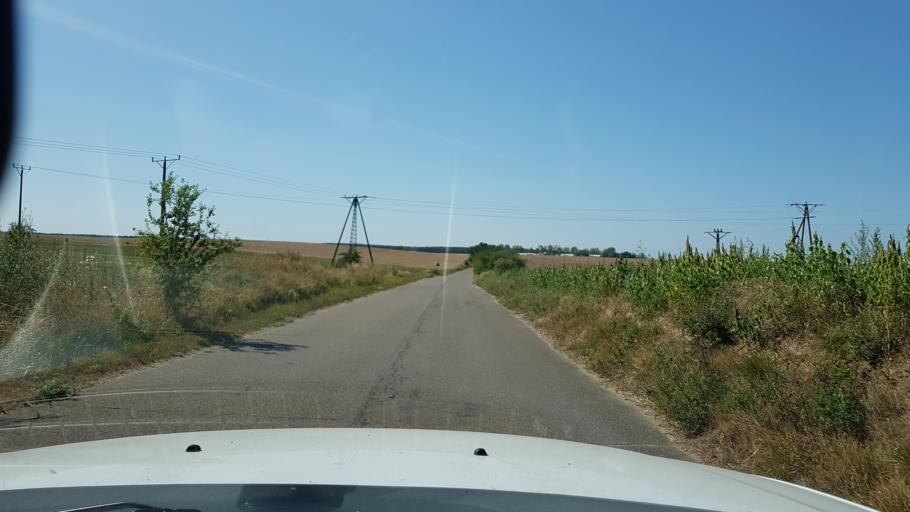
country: PL
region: West Pomeranian Voivodeship
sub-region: Powiat gryfinski
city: Moryn
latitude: 52.8470
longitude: 14.3853
